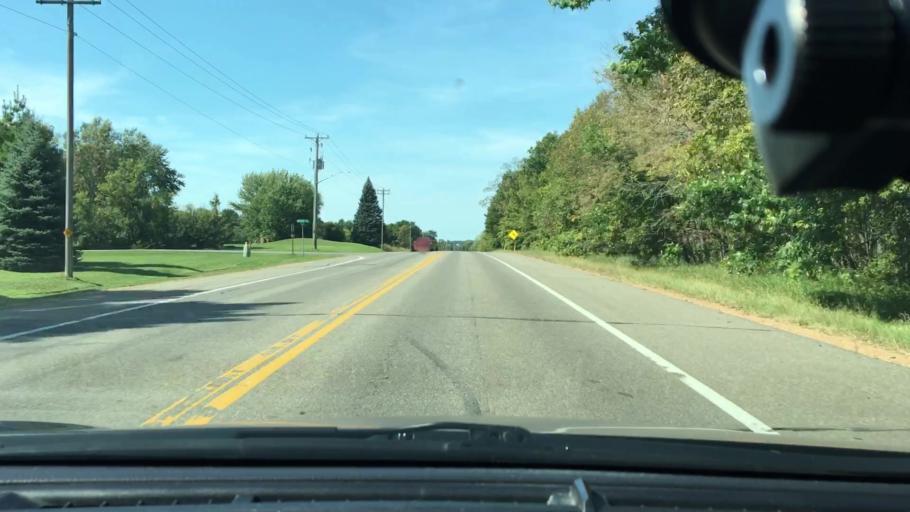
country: US
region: Minnesota
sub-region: Wright County
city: Hanover
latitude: 45.1526
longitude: -93.6384
